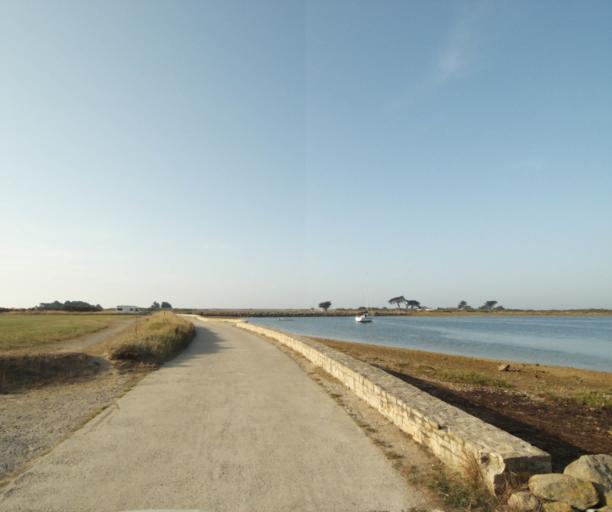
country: FR
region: Brittany
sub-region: Departement du Morbihan
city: Riantec
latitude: 47.7075
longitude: -3.3109
